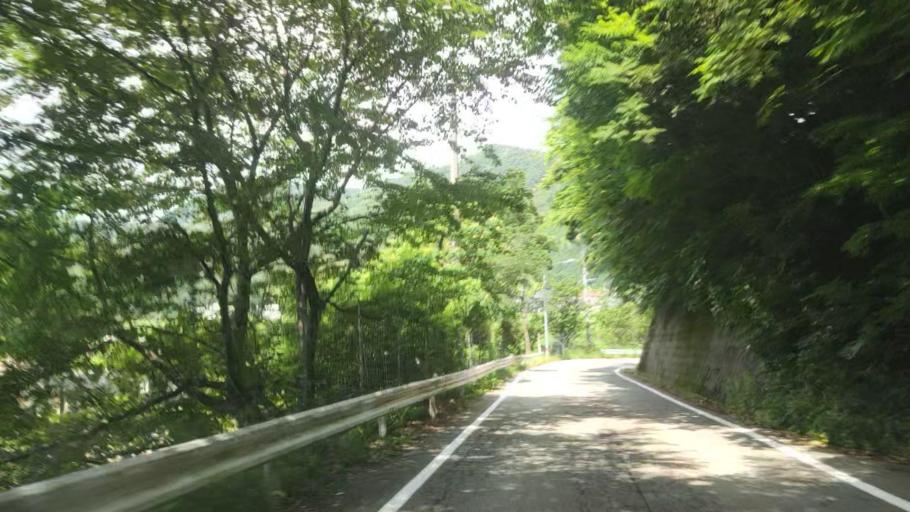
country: JP
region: Hyogo
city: Toyooka
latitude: 35.6423
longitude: 134.7633
